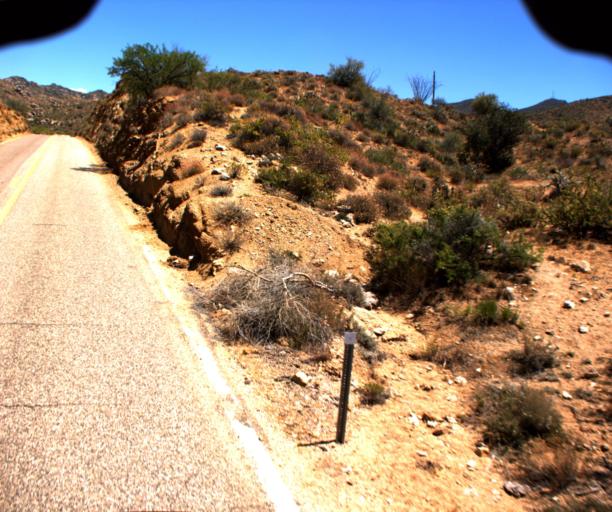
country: US
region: Arizona
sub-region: Yavapai County
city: Bagdad
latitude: 34.4535
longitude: -112.9899
